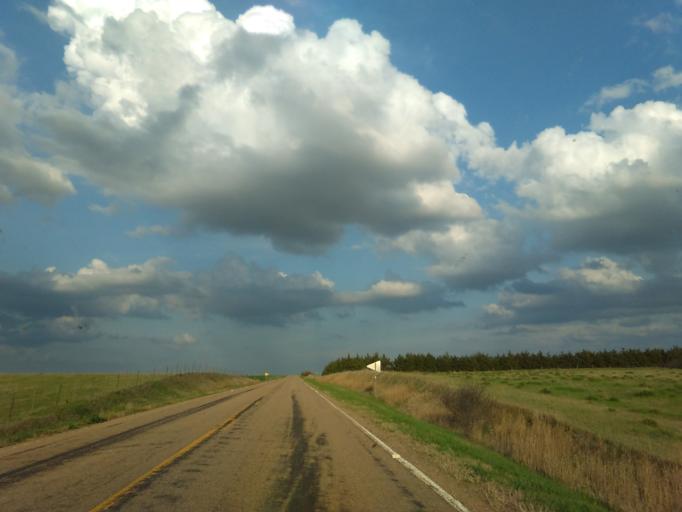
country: US
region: Nebraska
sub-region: Webster County
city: Red Cloud
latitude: 40.1760
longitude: -98.5122
